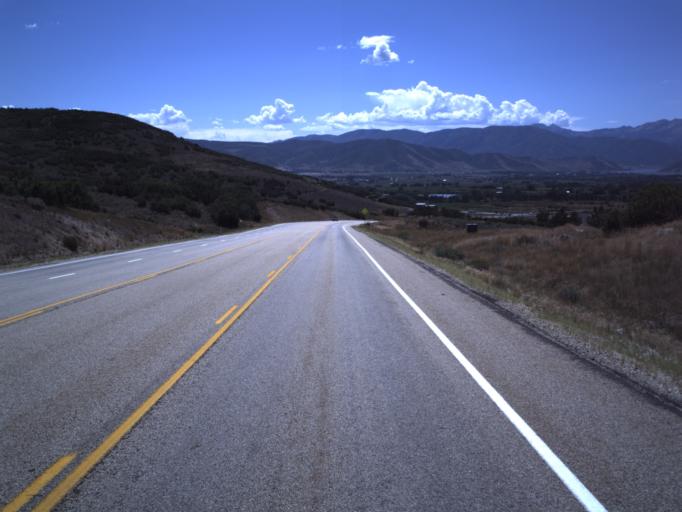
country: US
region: Utah
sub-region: Wasatch County
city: Heber
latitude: 40.5709
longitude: -111.4208
